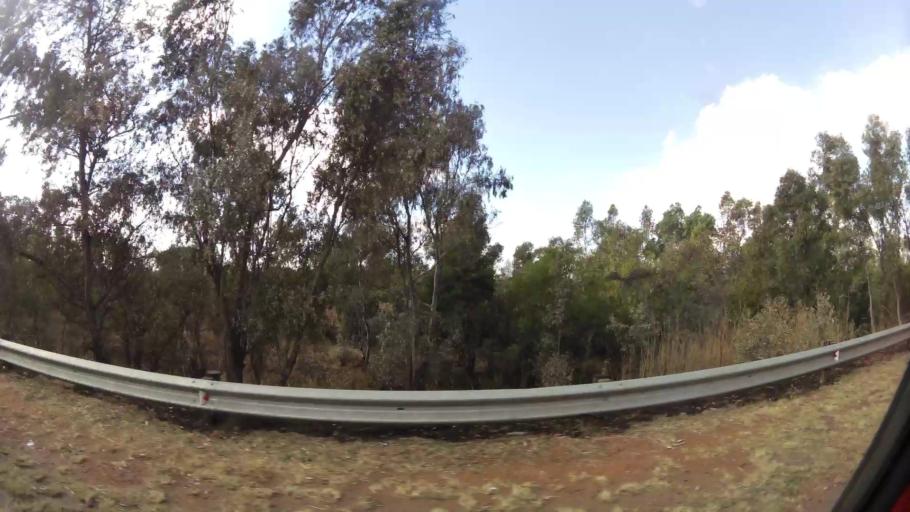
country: ZA
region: Gauteng
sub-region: Ekurhuleni Metropolitan Municipality
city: Tembisa
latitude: -25.9719
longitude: 28.2409
